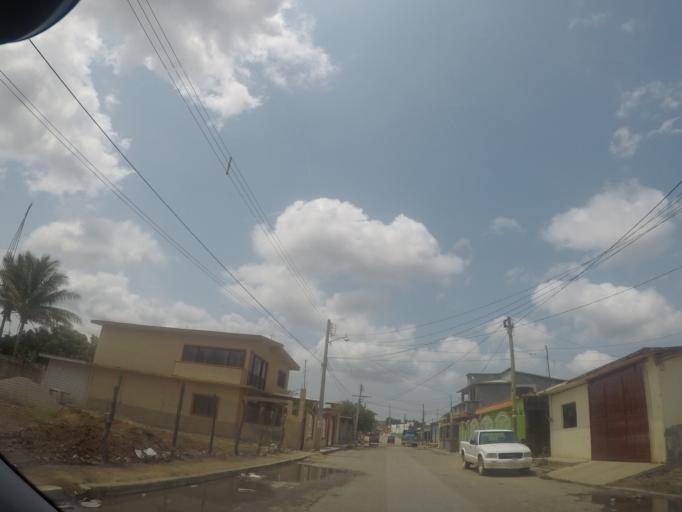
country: MX
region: Oaxaca
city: El Espinal
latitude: 16.5507
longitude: -94.9461
